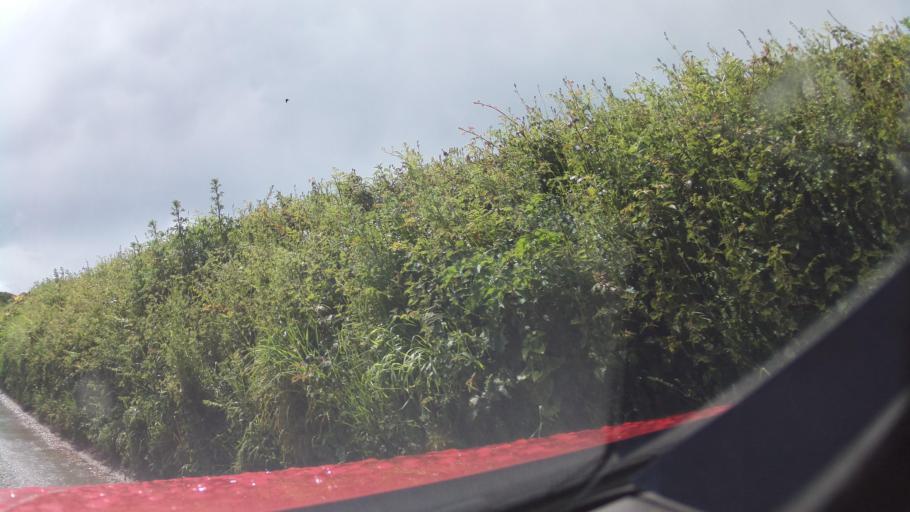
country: GB
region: England
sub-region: Devon
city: Dartmouth
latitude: 50.3534
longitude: -3.5390
